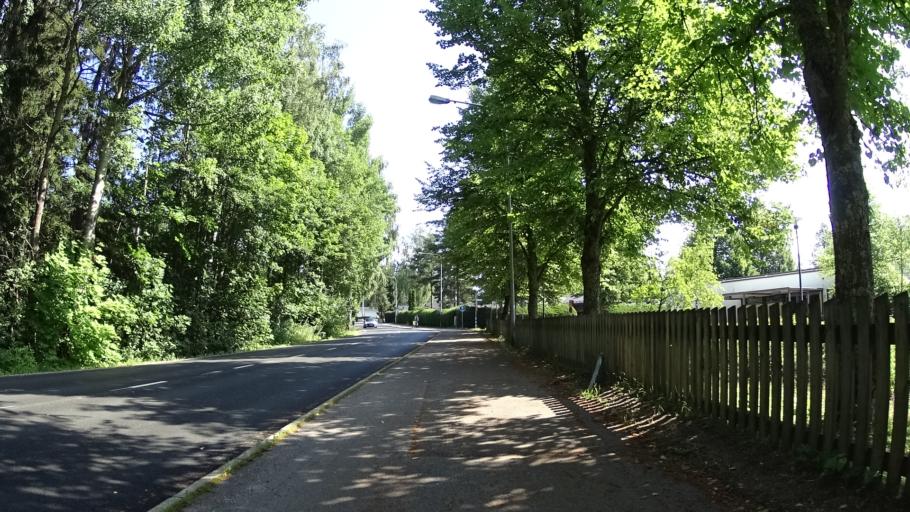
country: FI
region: Uusimaa
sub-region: Helsinki
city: Tuusula
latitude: 60.4071
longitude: 25.0264
